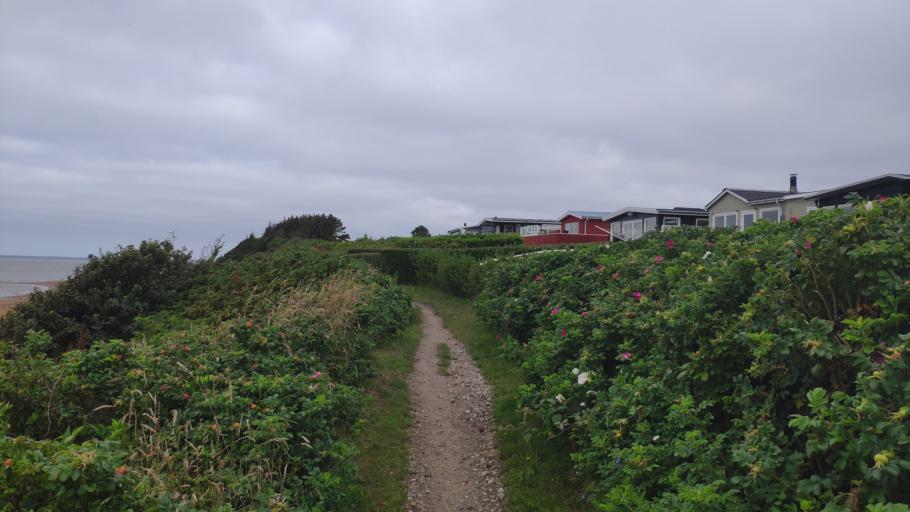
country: DK
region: South Denmark
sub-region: Varde Kommune
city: Oksbol
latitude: 55.5348
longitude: 8.3393
